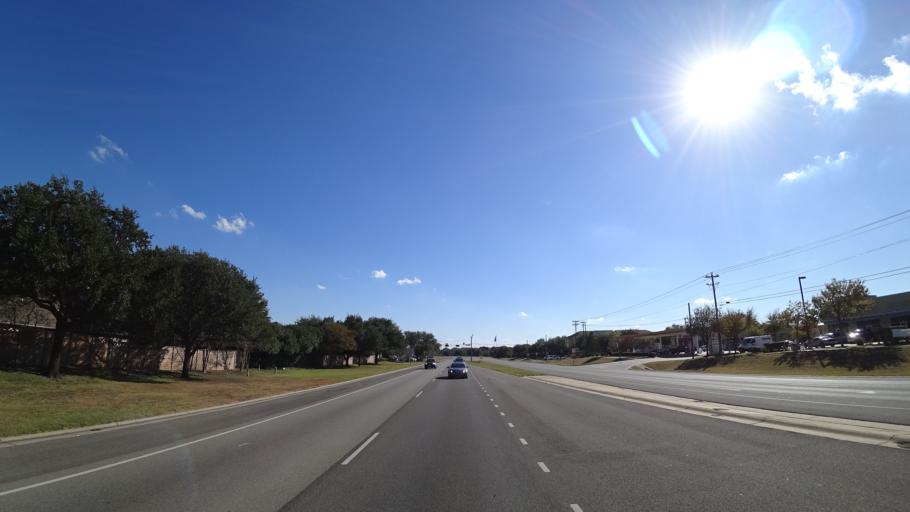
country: US
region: Texas
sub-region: Williamson County
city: Brushy Creek
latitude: 30.4891
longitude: -97.7717
